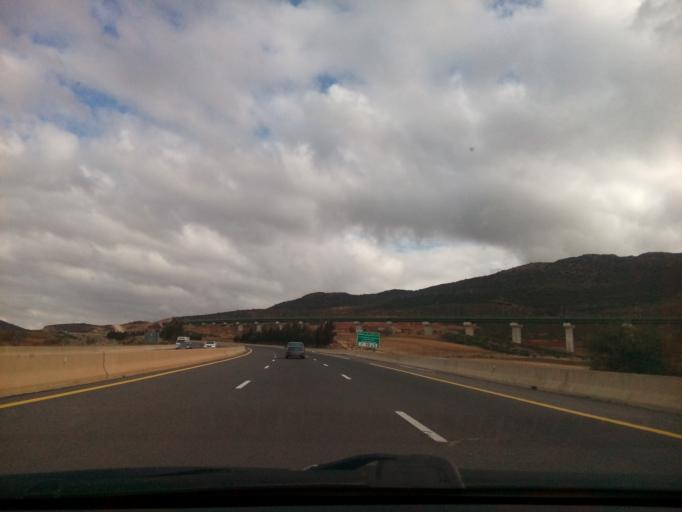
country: DZ
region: Tlemcen
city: Sidi Abdelli
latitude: 35.0094
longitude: -1.1657
